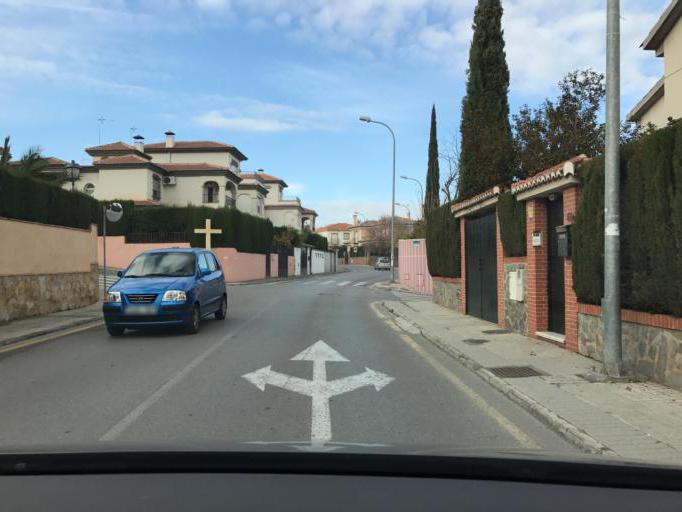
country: ES
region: Andalusia
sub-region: Provincia de Granada
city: Ogijares
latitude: 37.1148
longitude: -3.6112
